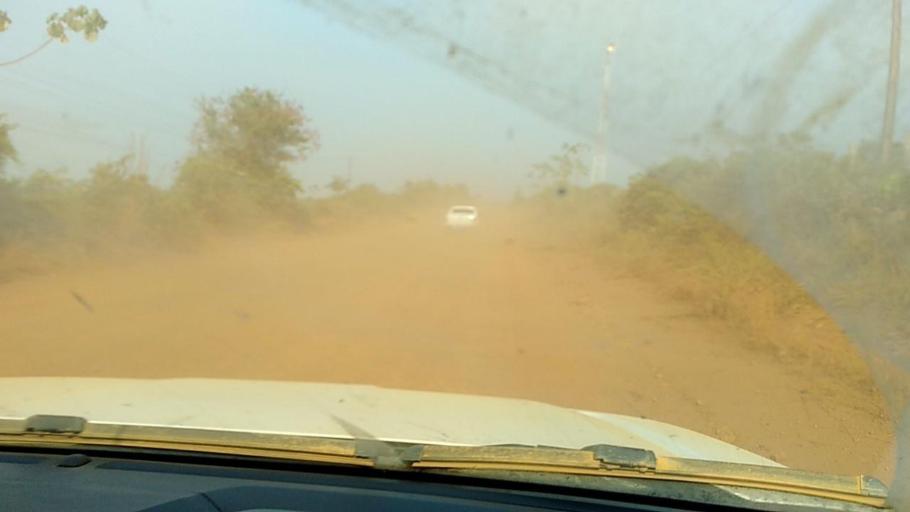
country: BR
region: Rondonia
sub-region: Porto Velho
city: Porto Velho
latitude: -8.7592
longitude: -63.9694
